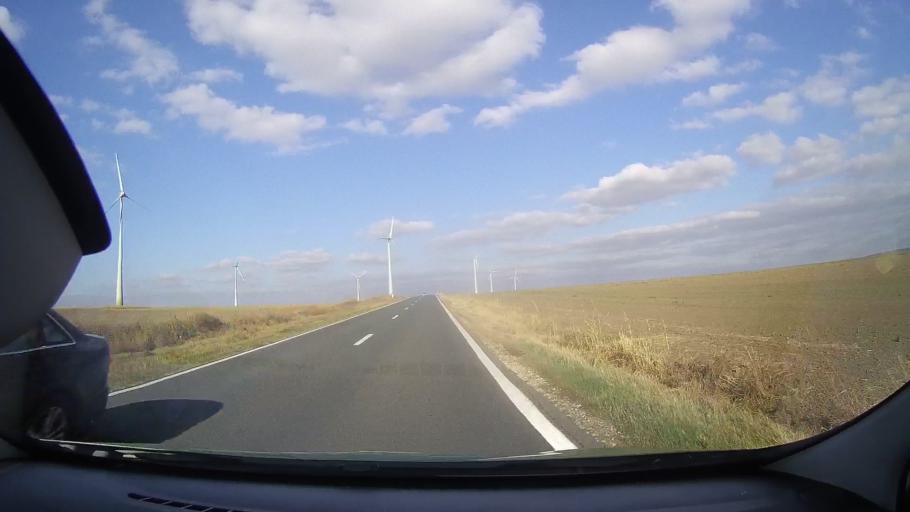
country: RO
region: Tulcea
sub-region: Comuna Topolog
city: Topolog
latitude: 44.8154
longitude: 28.2575
